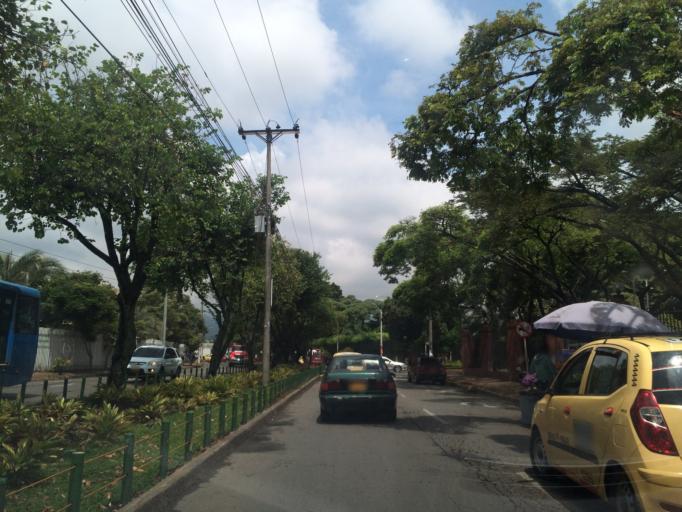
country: CO
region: Valle del Cauca
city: Cali
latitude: 3.3713
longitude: -76.5262
